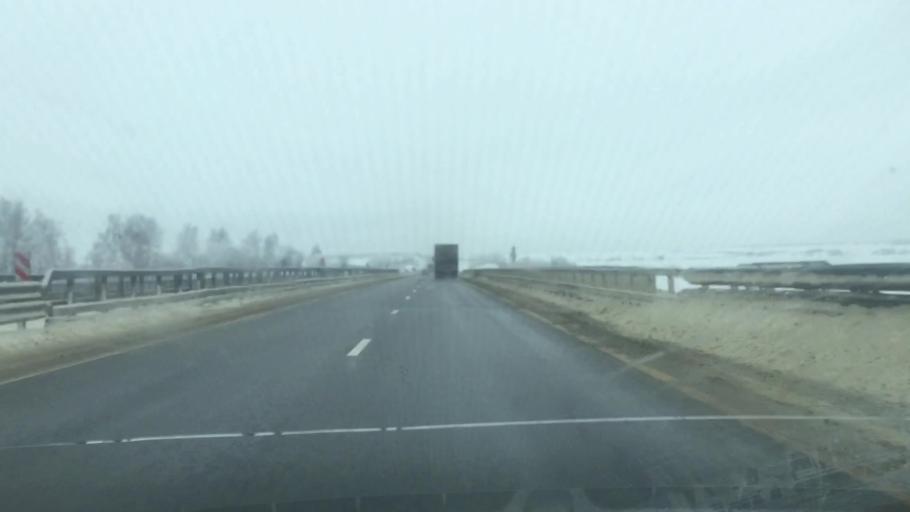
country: RU
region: Tula
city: Kazachka
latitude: 53.3385
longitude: 38.1809
